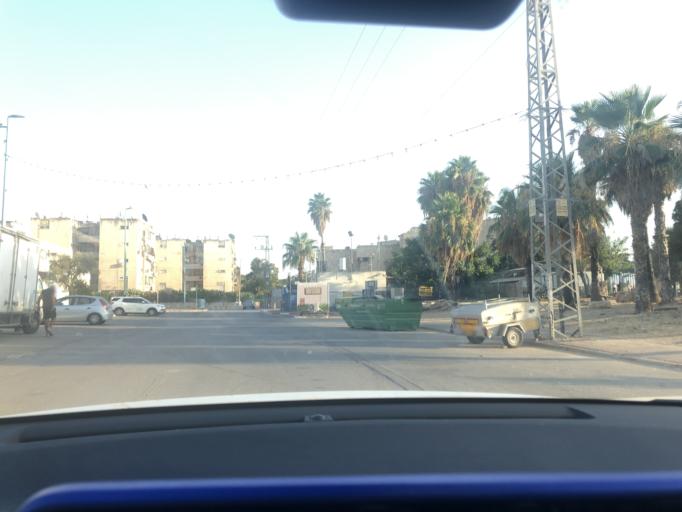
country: IL
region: Central District
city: Lod
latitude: 31.9545
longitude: 34.9013
